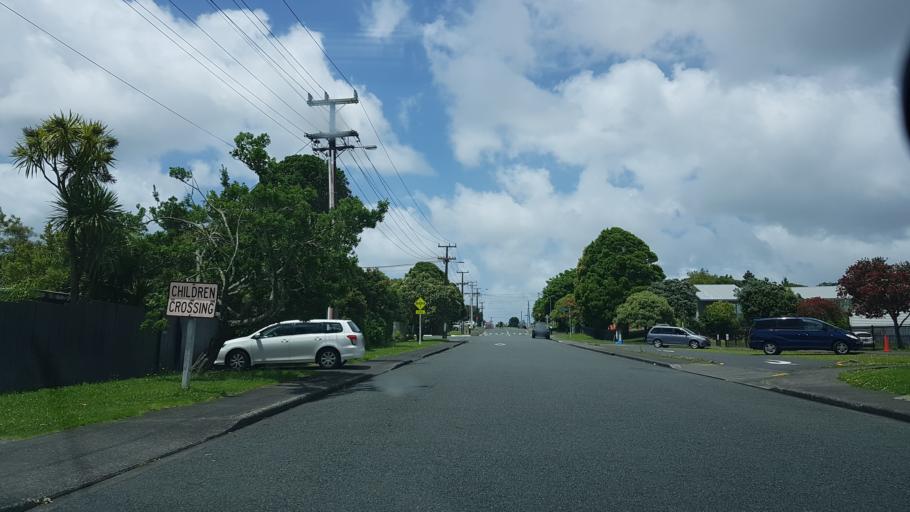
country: NZ
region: Auckland
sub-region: Auckland
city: North Shore
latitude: -36.7929
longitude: 174.6910
